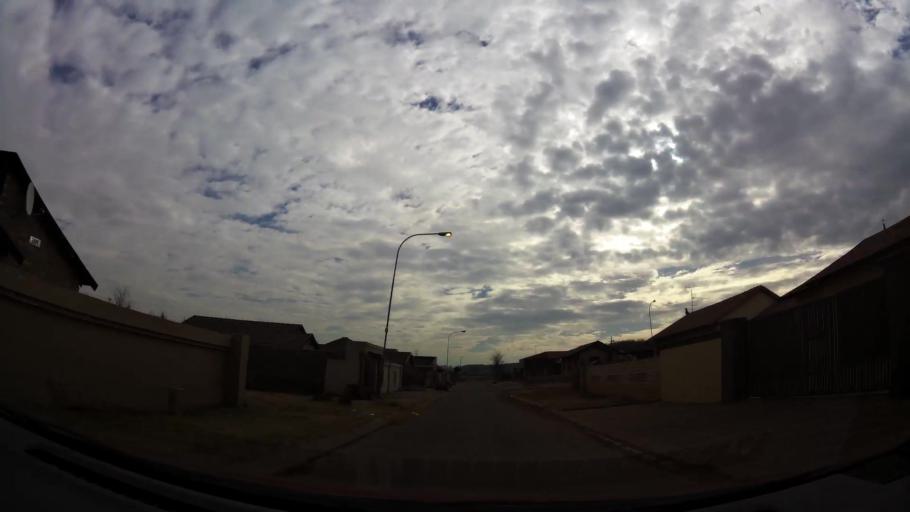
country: ZA
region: Gauteng
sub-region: City of Johannesburg Metropolitan Municipality
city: Soweto
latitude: -26.2718
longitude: 27.8392
